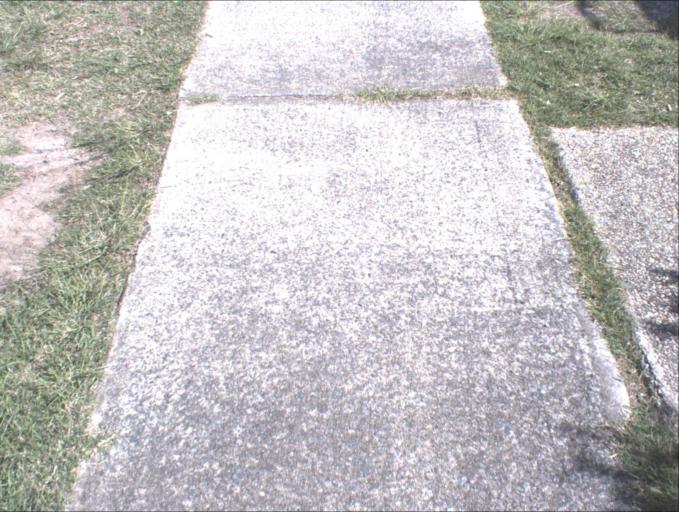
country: AU
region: Queensland
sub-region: Logan
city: Waterford West
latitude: -27.7002
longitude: 153.1643
